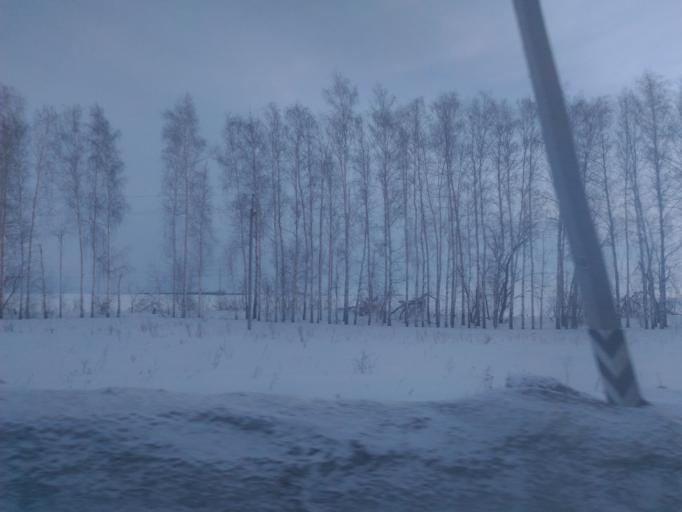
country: RU
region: Ulyanovsk
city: Isheyevka
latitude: 54.4107
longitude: 48.2954
